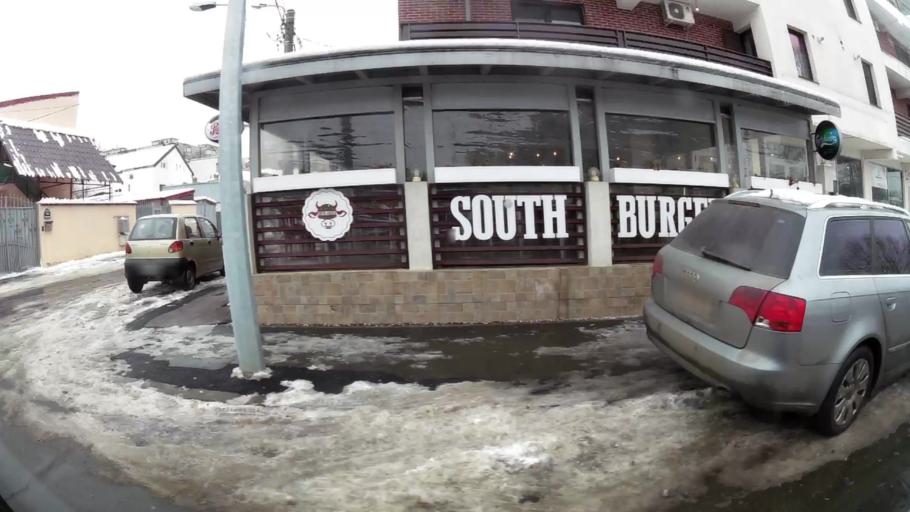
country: RO
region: Bucuresti
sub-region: Municipiul Bucuresti
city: Bucuresti
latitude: 44.3938
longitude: 26.1127
